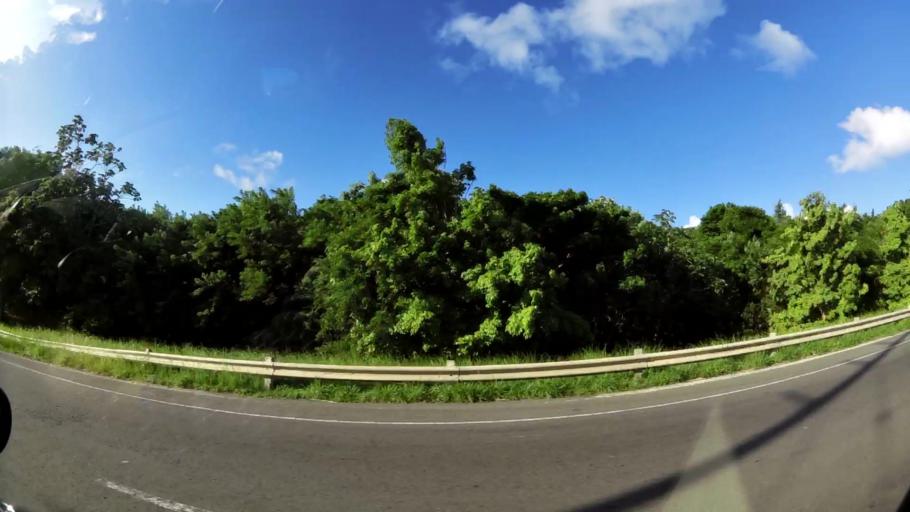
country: TT
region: Tobago
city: Scarborough
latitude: 11.1795
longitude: -60.7070
